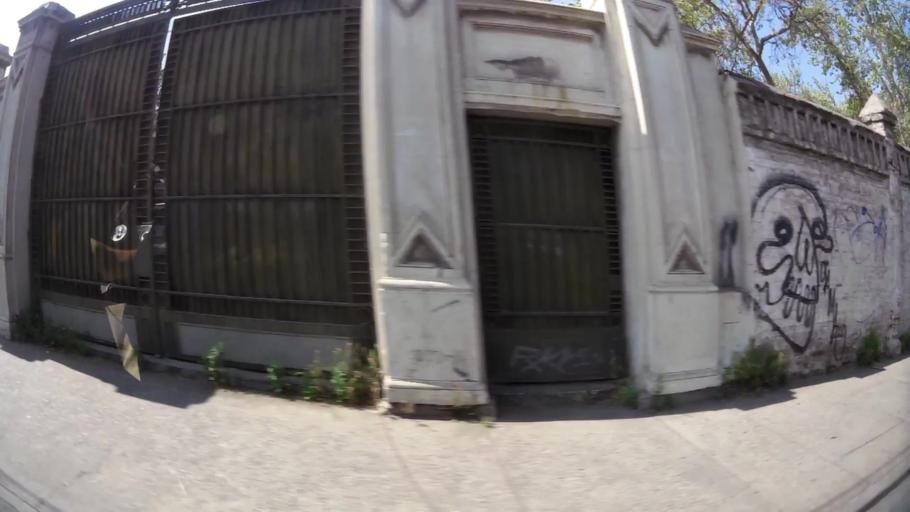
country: CL
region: Santiago Metropolitan
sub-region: Provincia de Santiago
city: Santiago
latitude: -33.4613
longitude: -70.6717
